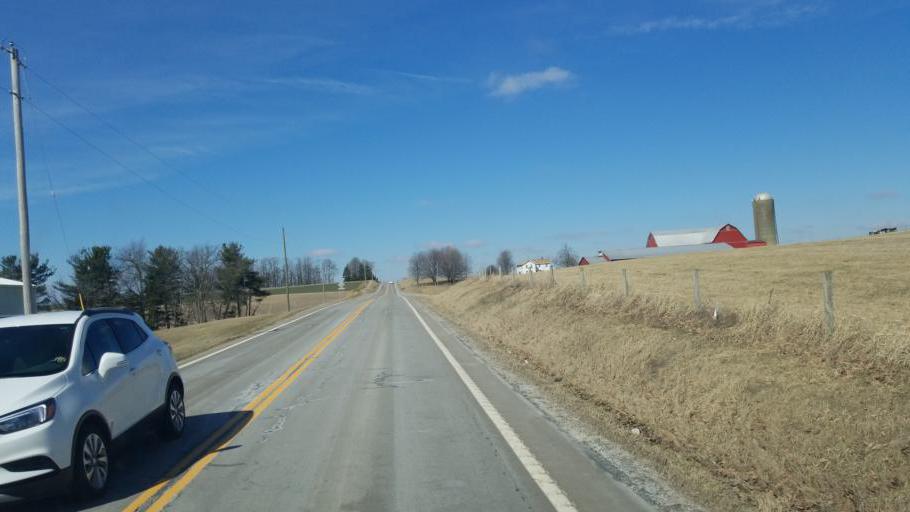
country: US
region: Ohio
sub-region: Ashland County
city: Loudonville
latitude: 40.7268
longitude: -82.2409
